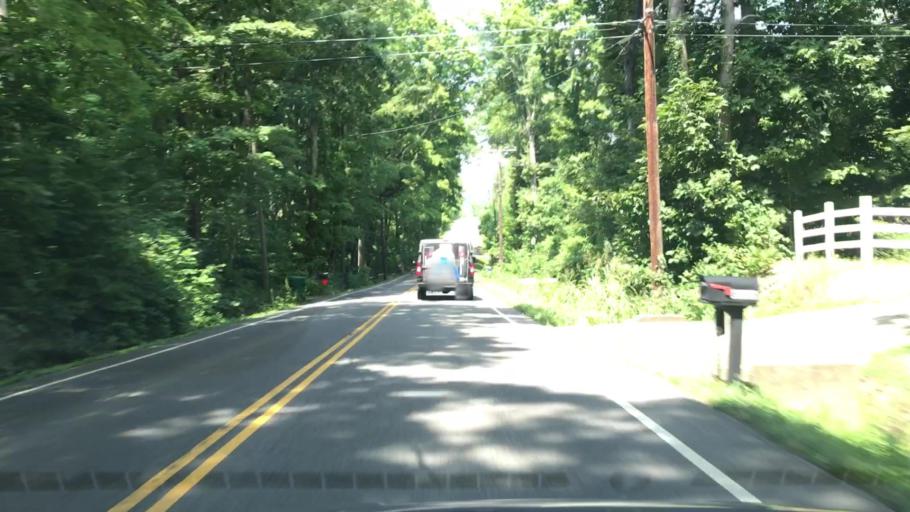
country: US
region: Tennessee
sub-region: Williamson County
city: Nolensville
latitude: 35.9910
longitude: -86.6440
